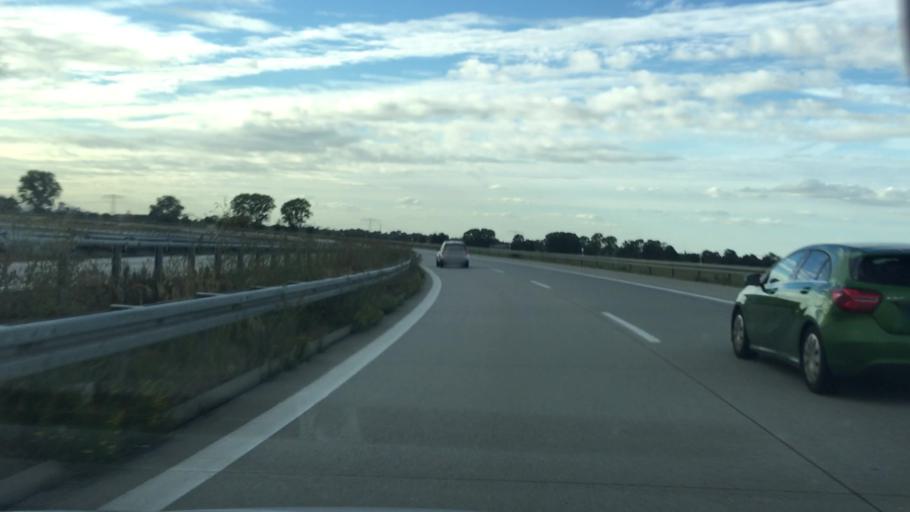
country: DE
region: Saxony
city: Borsdorf
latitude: 51.3134
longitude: 12.5526
